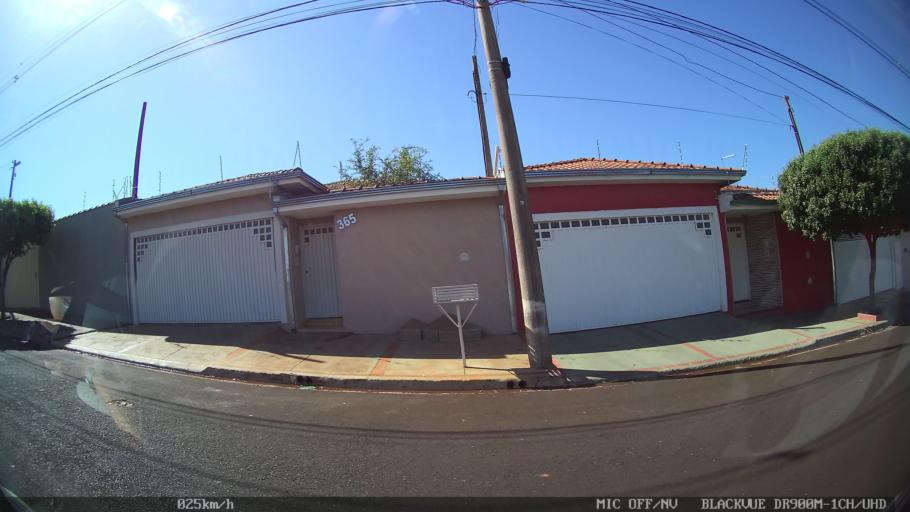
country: BR
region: Sao Paulo
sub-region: Batatais
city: Batatais
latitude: -20.8881
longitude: -47.5655
